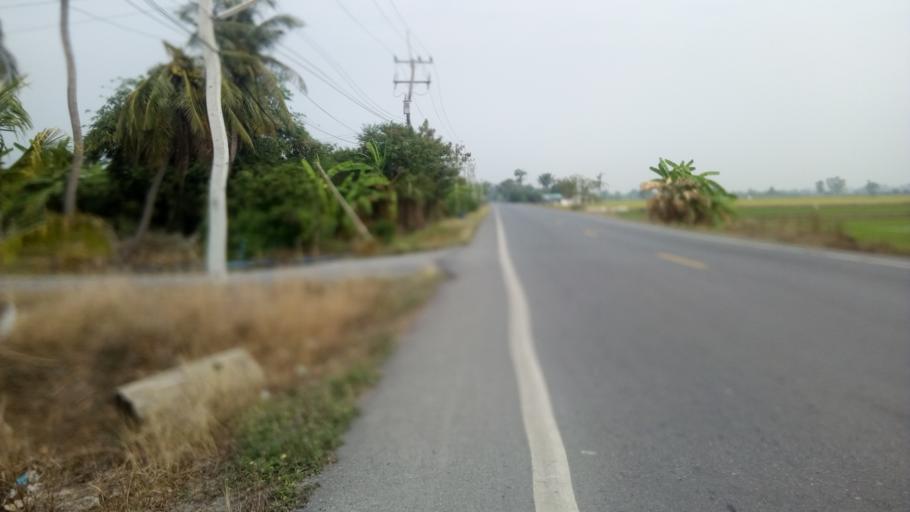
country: TH
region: Pathum Thani
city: Ban Rangsit
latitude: 14.0273
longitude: 100.8242
